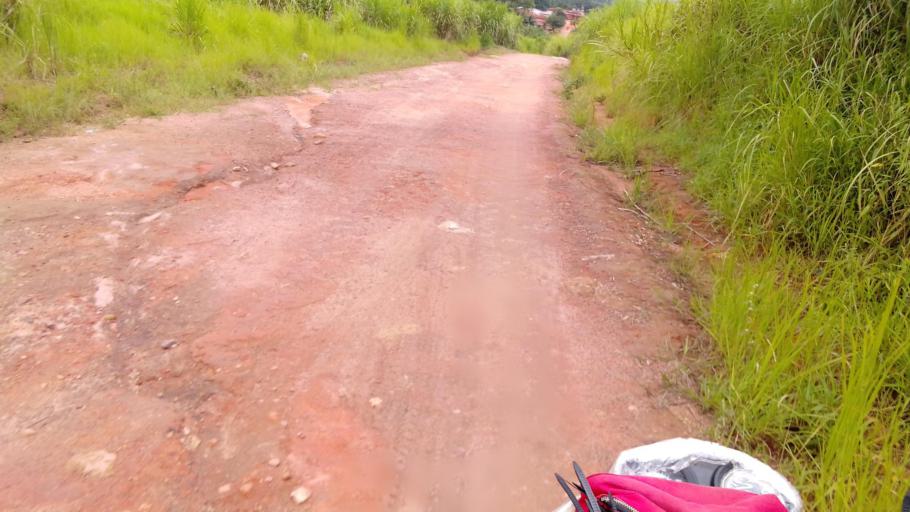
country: SL
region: Eastern Province
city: Koidu
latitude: 8.6854
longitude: -10.9311
